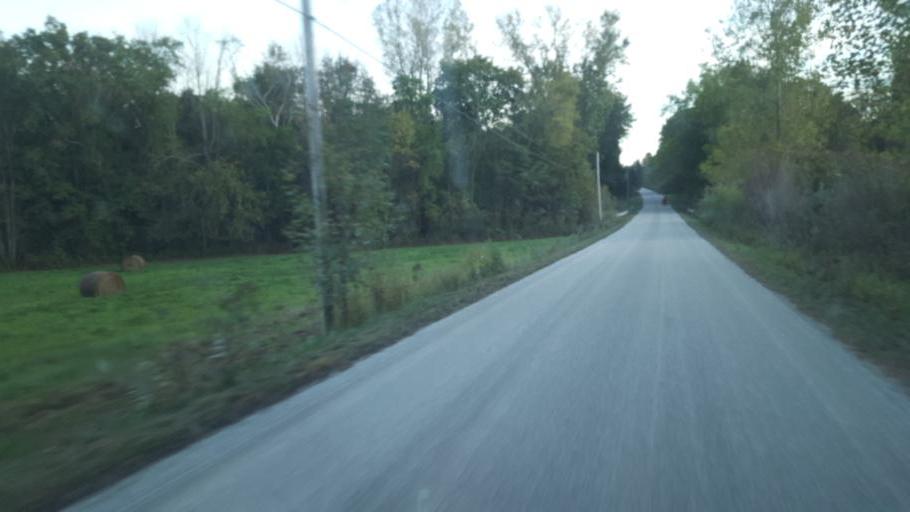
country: US
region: Ohio
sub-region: Richland County
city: Lexington
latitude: 40.6223
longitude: -82.6509
